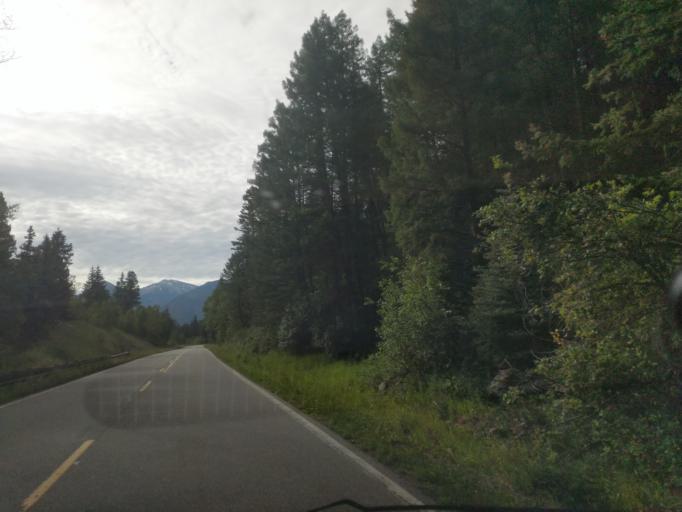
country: US
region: Colorado
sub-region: Garfield County
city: Carbondale
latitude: 39.0913
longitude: -107.2532
